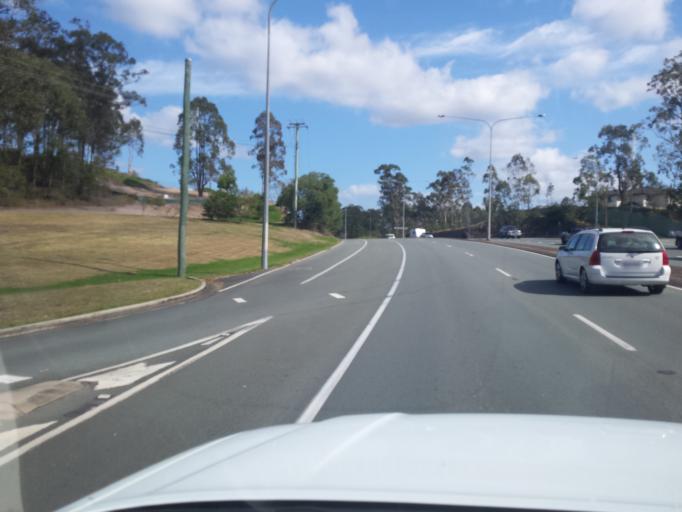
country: AU
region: Queensland
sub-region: Brisbane
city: Bridegman Downs
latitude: -27.3687
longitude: 152.9789
